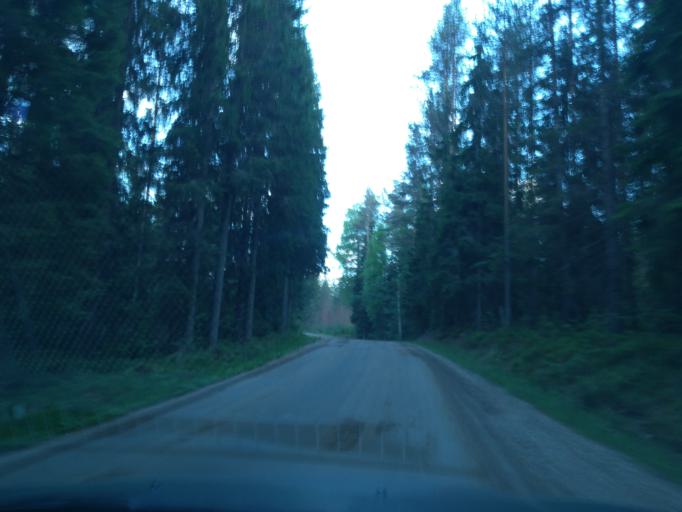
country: FI
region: Southern Savonia
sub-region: Mikkeli
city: Puumala
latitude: 61.6258
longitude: 28.1081
